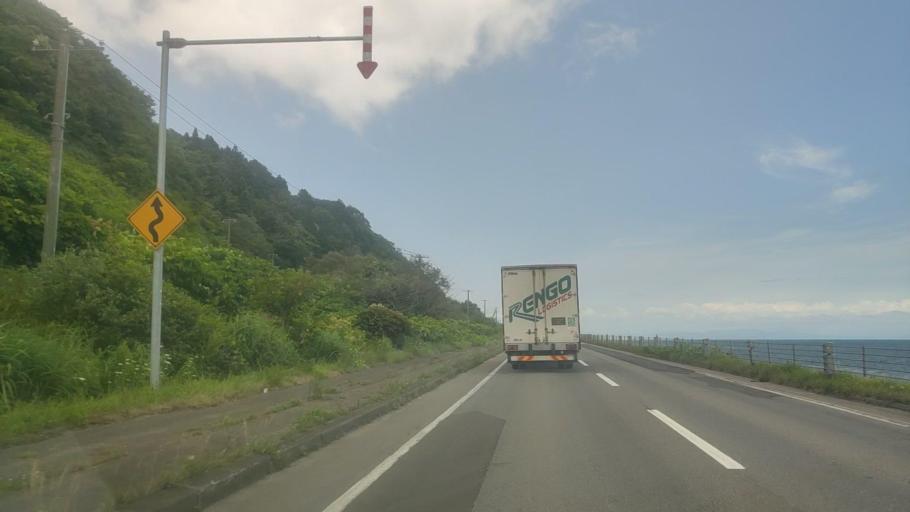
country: JP
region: Hokkaido
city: Nanae
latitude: 42.1497
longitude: 140.4941
